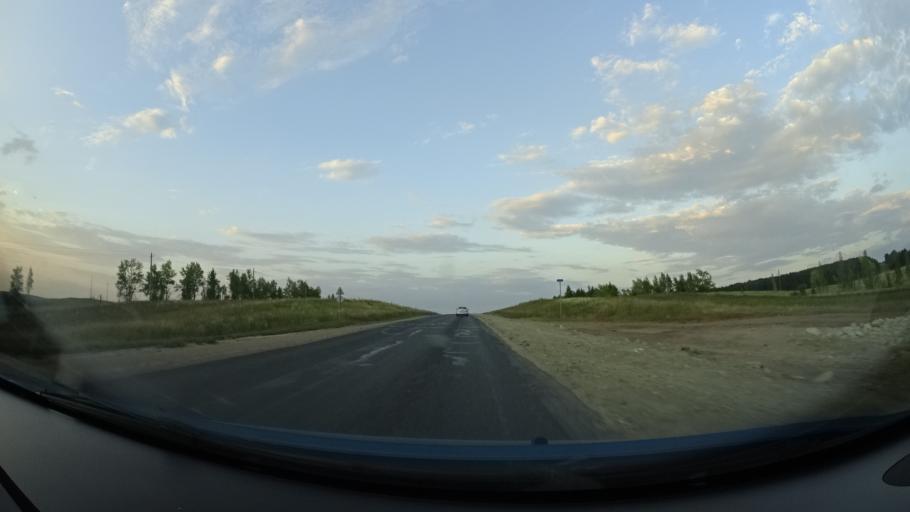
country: RU
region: Orenburg
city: Severnoye
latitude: 54.2149
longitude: 52.7173
